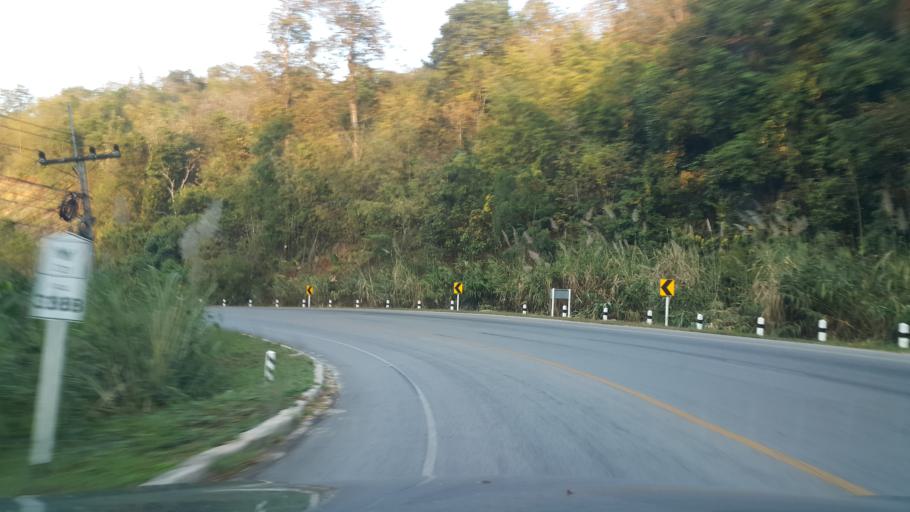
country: TH
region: Loei
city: Phu Ruea
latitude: 17.4773
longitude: 101.5391
